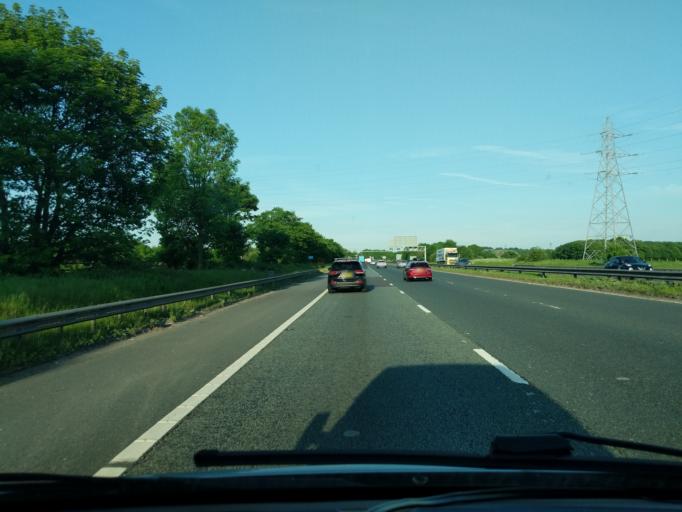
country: GB
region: England
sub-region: Knowsley
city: Whiston
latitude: 53.4012
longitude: -2.7815
